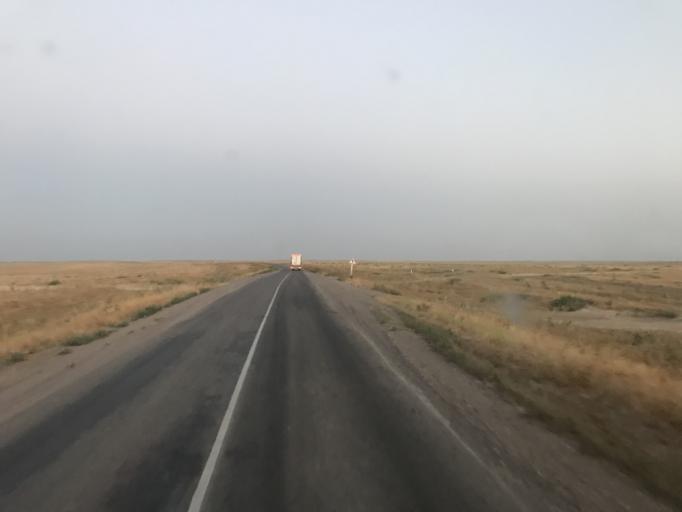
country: UZ
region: Toshkent
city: Chinoz
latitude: 41.1816
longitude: 68.6304
